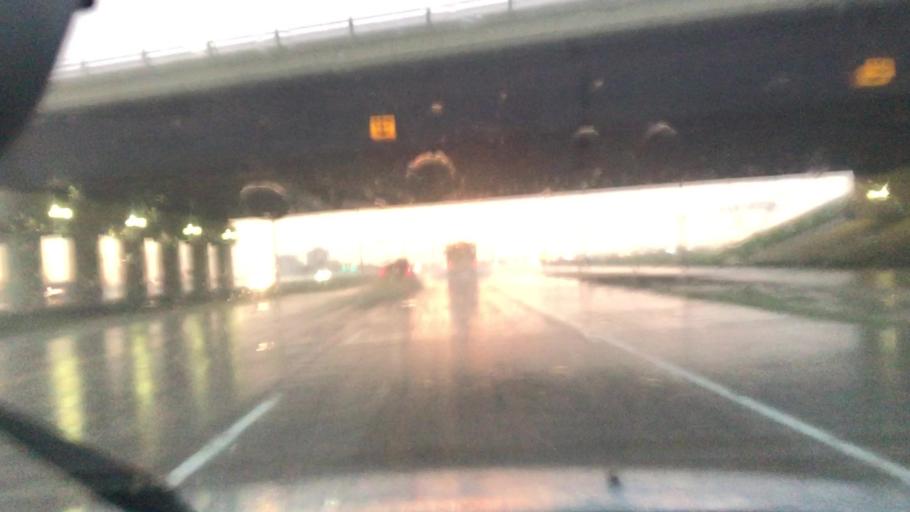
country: CA
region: Alberta
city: Edmonton
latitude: 53.4306
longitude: -113.5821
